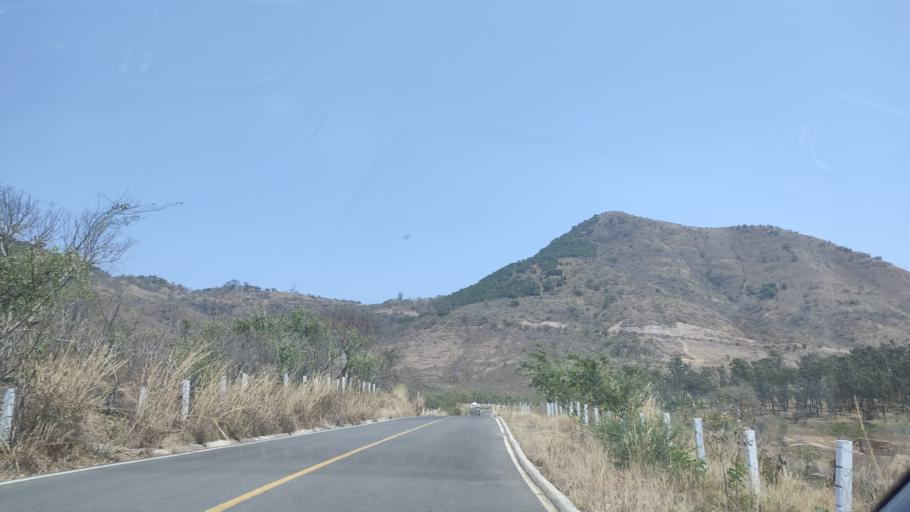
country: MX
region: Nayarit
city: Puga
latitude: 21.6128
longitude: -104.7233
